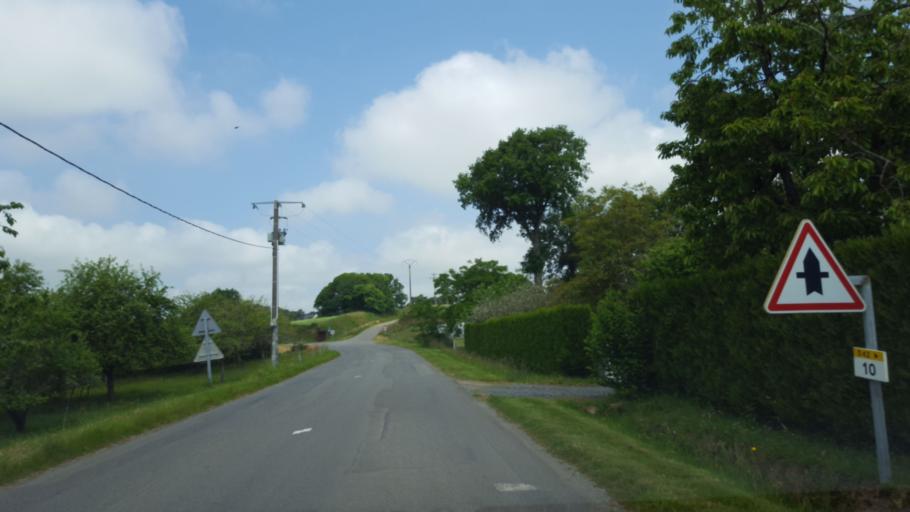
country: FR
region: Brittany
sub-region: Departement d'Ille-et-Vilaine
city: Baulon
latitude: 47.9260
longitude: -1.9231
